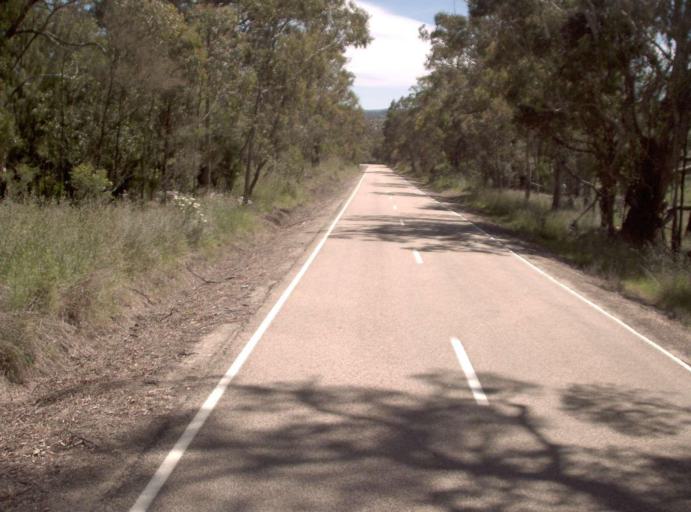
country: AU
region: Victoria
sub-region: East Gippsland
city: Lakes Entrance
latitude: -37.2763
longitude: 148.2554
